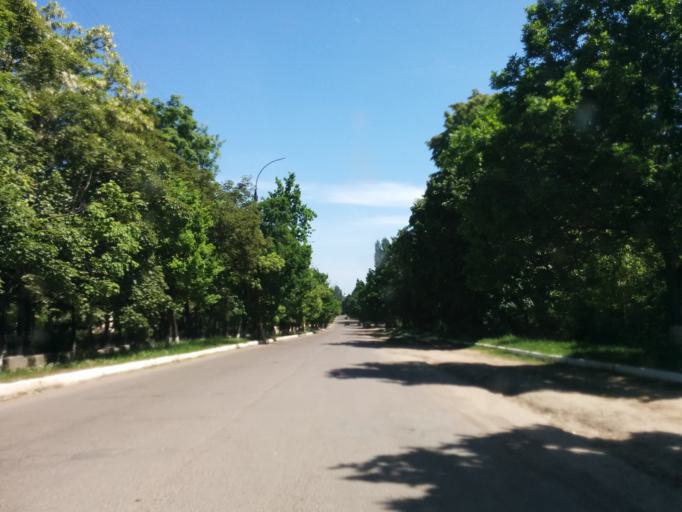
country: MD
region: Raionul Soroca
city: Soroca
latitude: 48.1622
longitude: 28.2833
